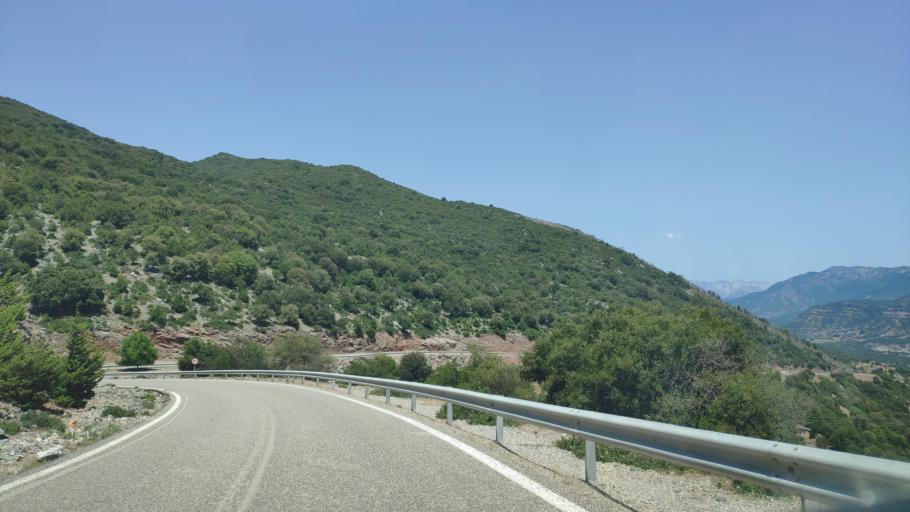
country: GR
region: Central Greece
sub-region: Nomos Evrytanias
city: Kerasochori
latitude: 39.0893
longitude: 21.4126
